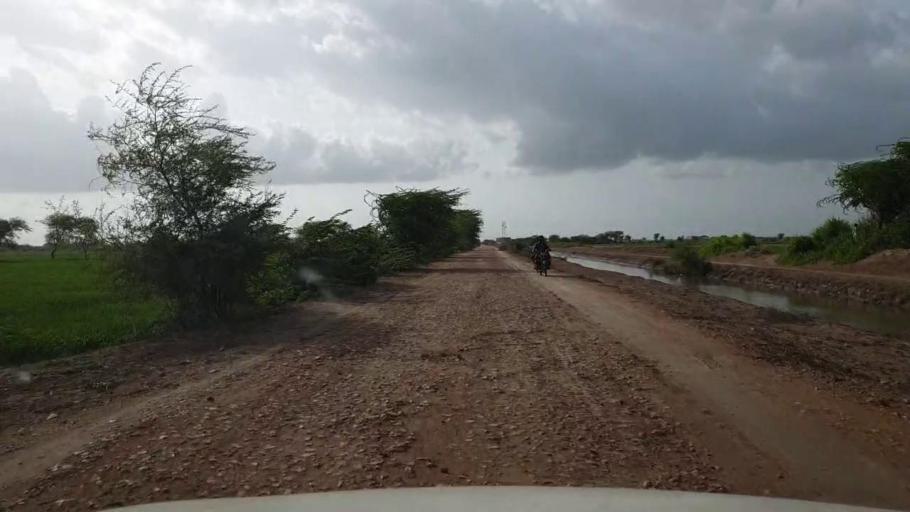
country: PK
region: Sindh
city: Kario
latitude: 24.7909
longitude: 68.5796
